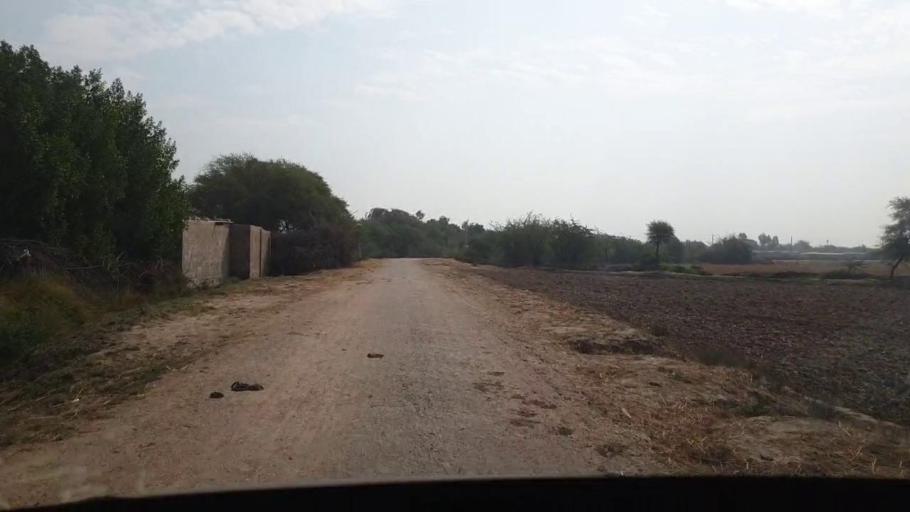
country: PK
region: Sindh
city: Chuhar Jamali
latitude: 24.3197
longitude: 67.9436
